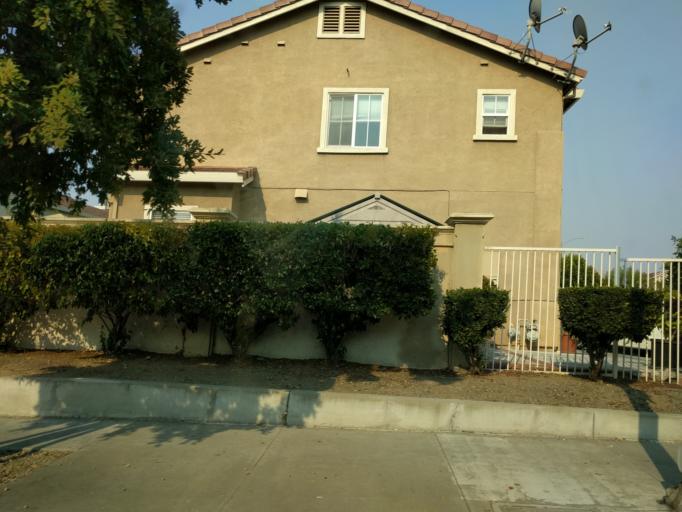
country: US
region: California
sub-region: Santa Clara County
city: Alum Rock
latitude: 37.3673
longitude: -121.8400
